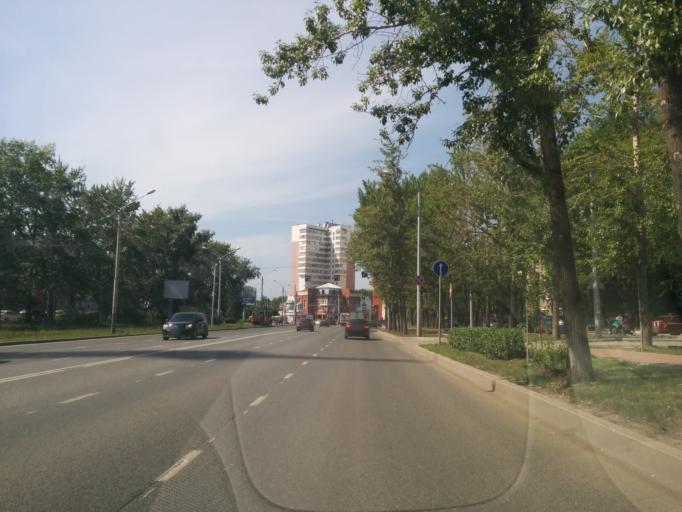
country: RU
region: Perm
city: Perm
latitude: 57.9936
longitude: 56.2902
